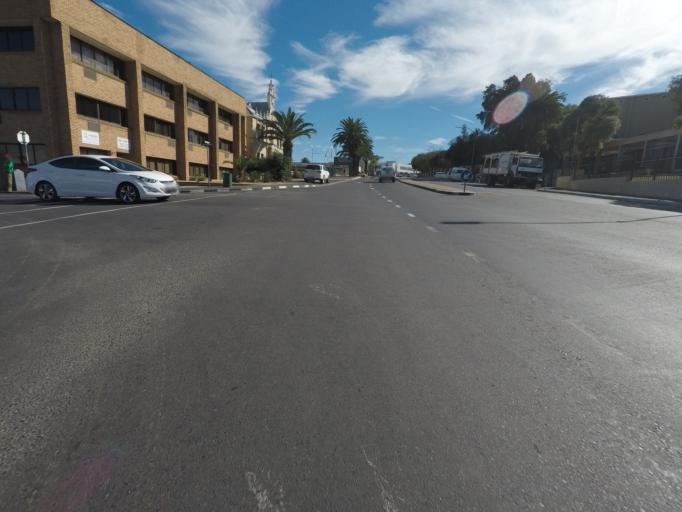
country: ZA
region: Western Cape
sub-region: West Coast District Municipality
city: Malmesbury
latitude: -33.4641
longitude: 18.7291
